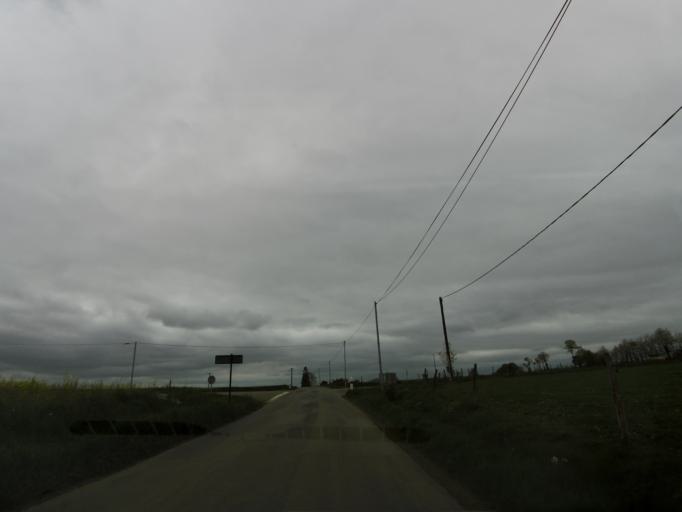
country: FR
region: Brittany
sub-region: Departement d'Ille-et-Vilaine
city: Janze
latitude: 47.9951
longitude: -1.5227
